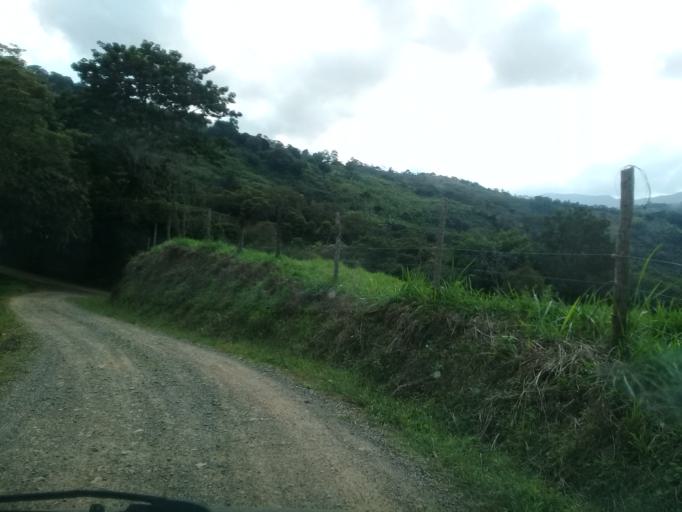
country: CO
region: Cundinamarca
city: Chaguani
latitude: 5.0055
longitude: -74.5882
